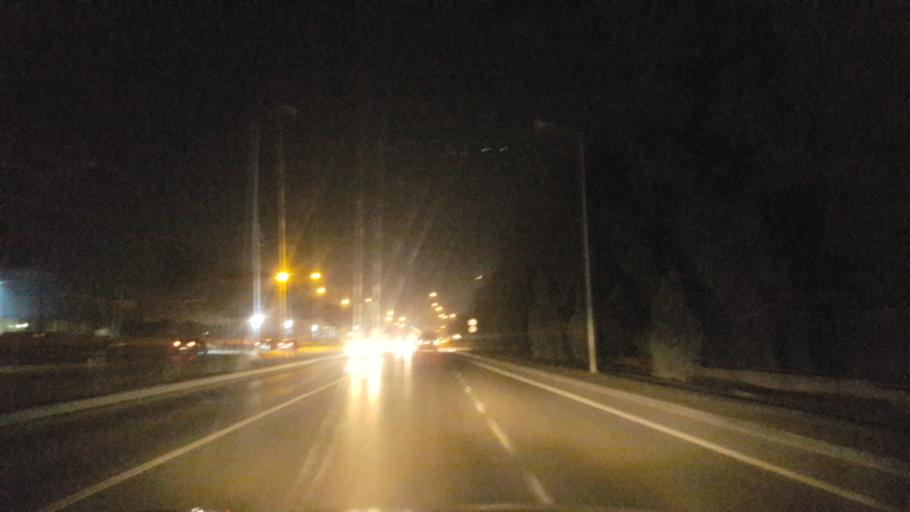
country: TR
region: Kocaeli
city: Gebze
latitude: 40.7999
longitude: 29.4547
